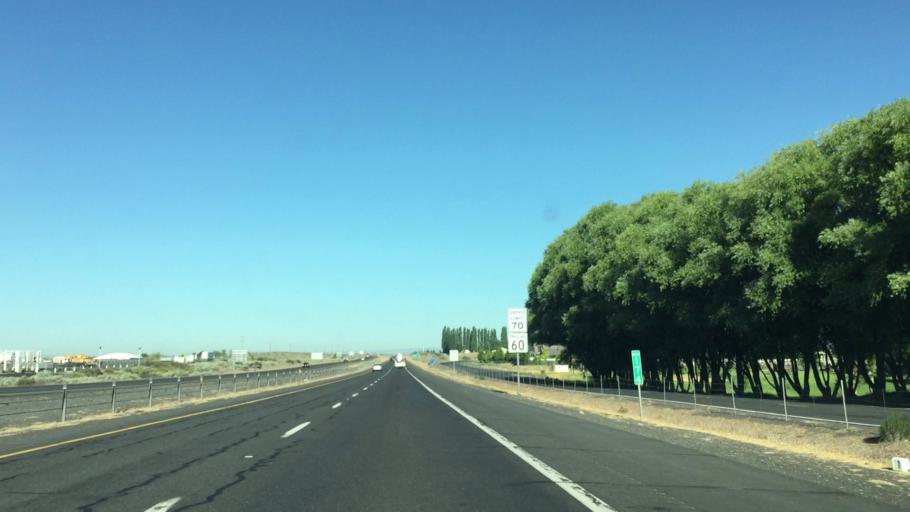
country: US
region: Washington
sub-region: Grant County
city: Cascade Valley
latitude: 47.1044
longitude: -119.3576
